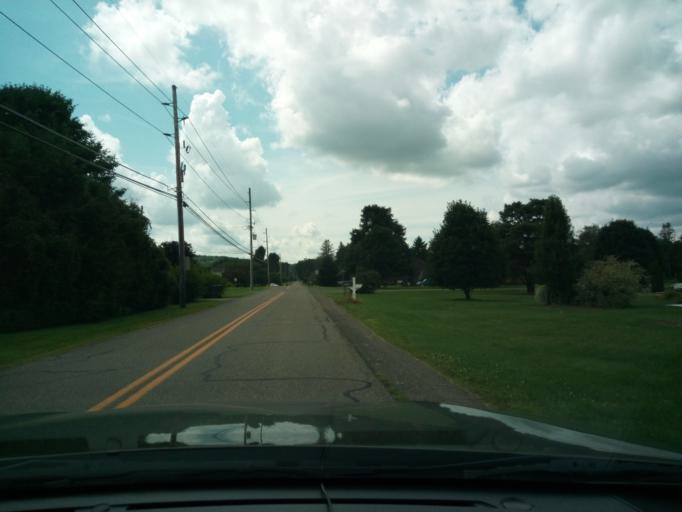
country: US
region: Pennsylvania
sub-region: Bradford County
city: South Waverly
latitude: 41.9959
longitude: -76.5711
